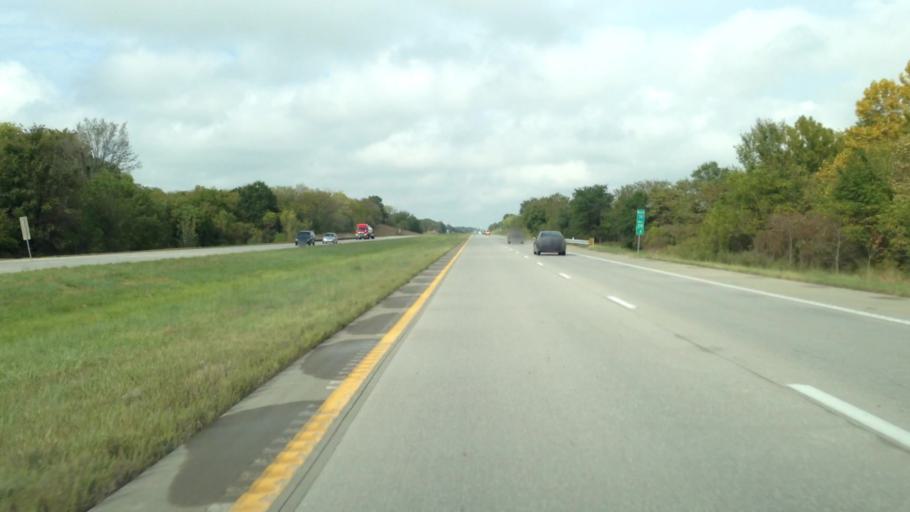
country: US
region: Missouri
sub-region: Clay County
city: Kearney
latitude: 39.3972
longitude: -94.3564
